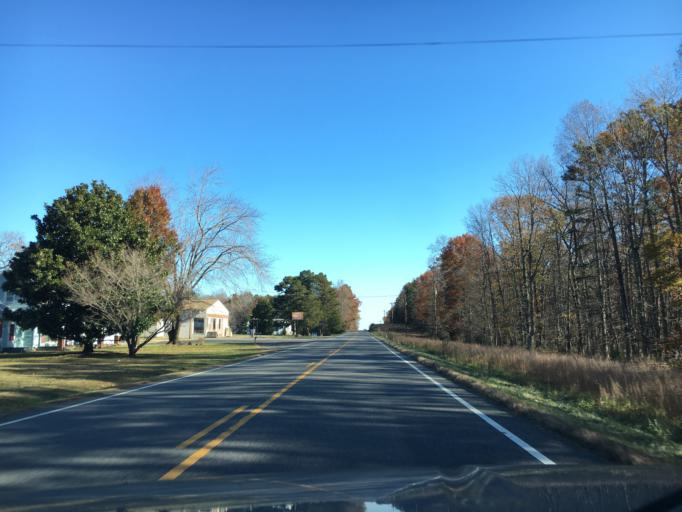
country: US
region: Virginia
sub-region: Buckingham County
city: Buckingham
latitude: 37.4643
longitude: -78.6692
